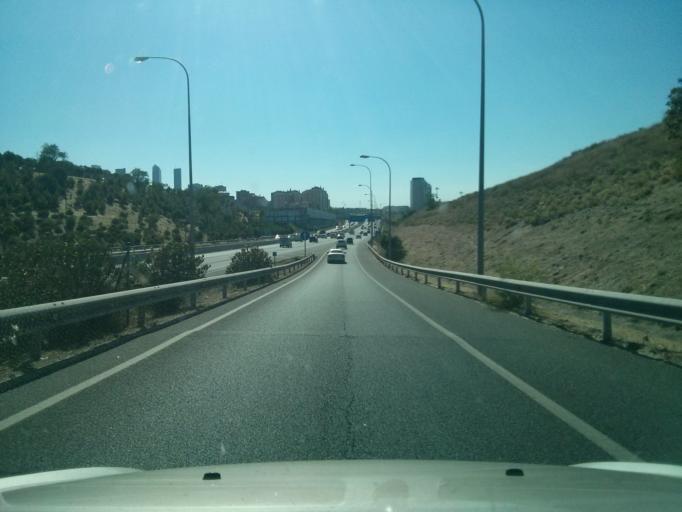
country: ES
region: Madrid
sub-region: Provincia de Madrid
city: Hortaleza
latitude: 40.4818
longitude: -3.6514
